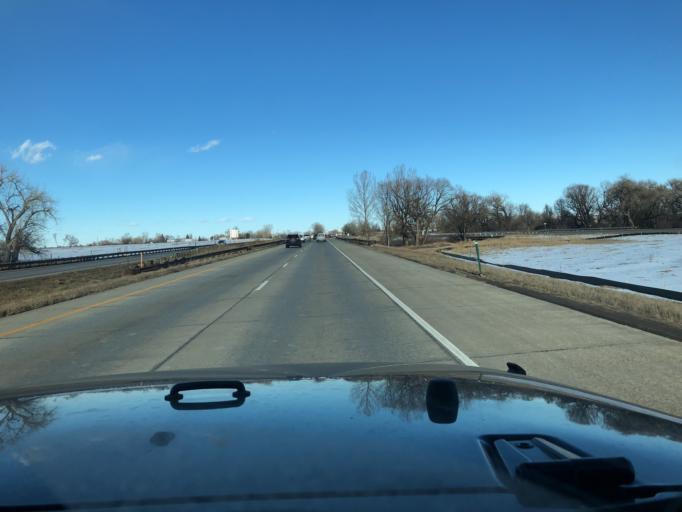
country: US
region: Colorado
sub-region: Boulder County
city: Boulder
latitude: 40.0445
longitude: -105.2415
